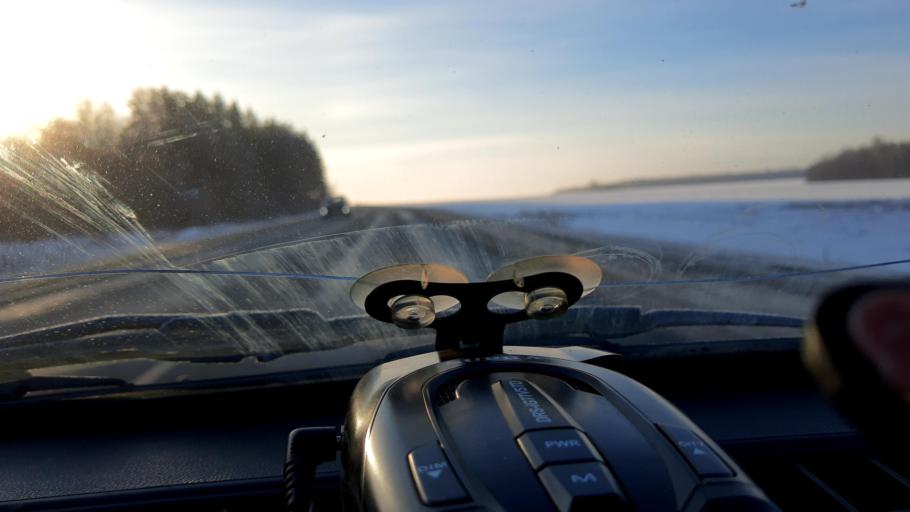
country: RU
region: Bashkortostan
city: Avdon
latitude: 54.7533
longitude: 55.7811
